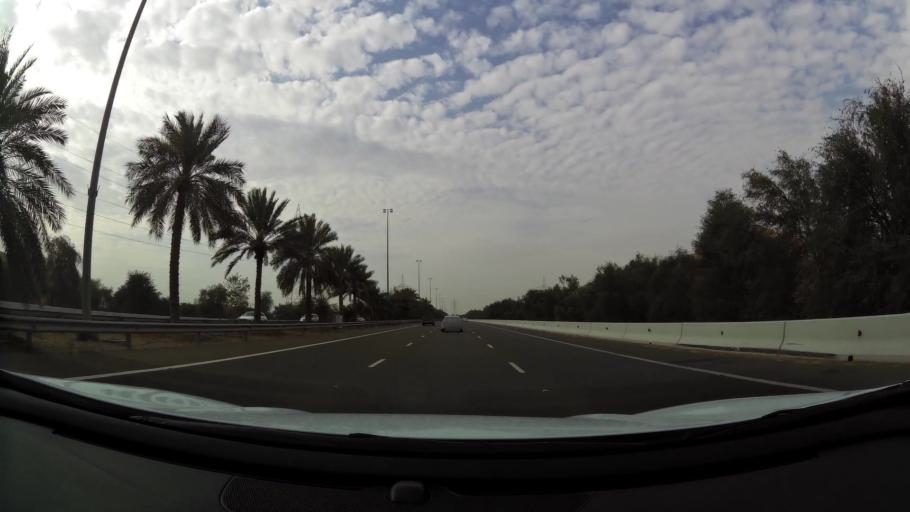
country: AE
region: Abu Dhabi
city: Al Ain
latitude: 24.2155
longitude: 55.5668
